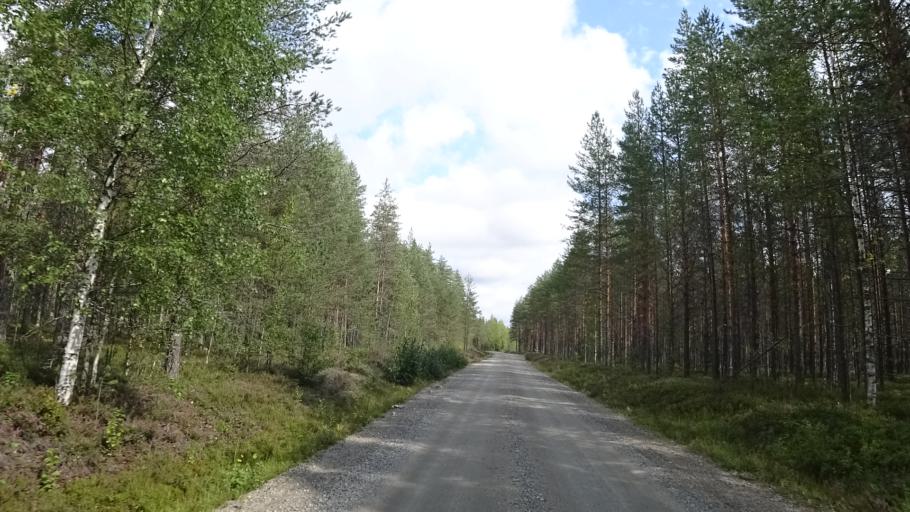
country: FI
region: North Karelia
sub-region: Joensuu
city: Ilomantsi
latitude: 62.9309
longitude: 31.4171
